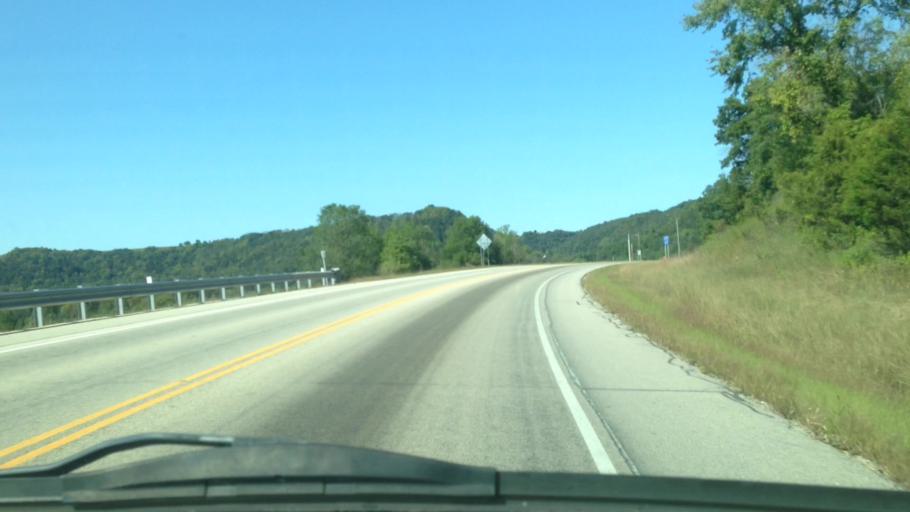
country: US
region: Minnesota
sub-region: Fillmore County
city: Rushford
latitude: 43.8298
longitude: -91.7666
